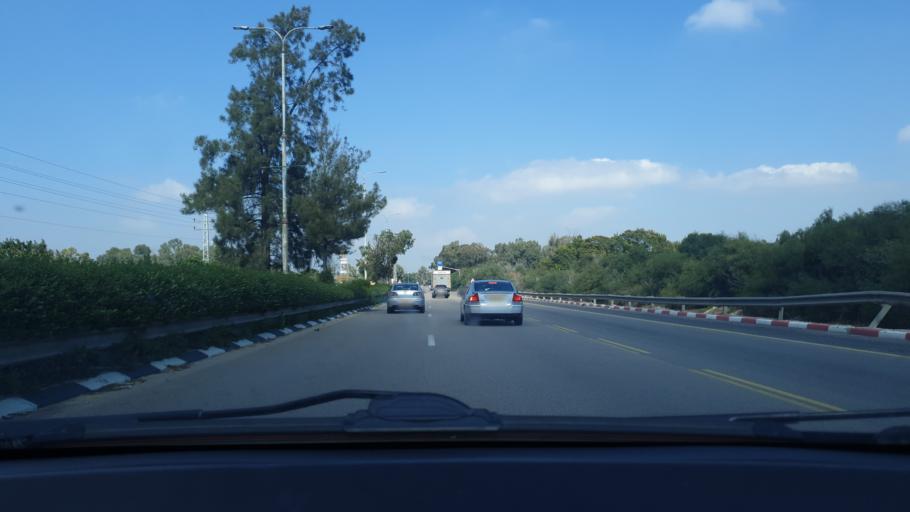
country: IL
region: Central District
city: Bet Dagan
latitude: 31.9873
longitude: 34.8116
